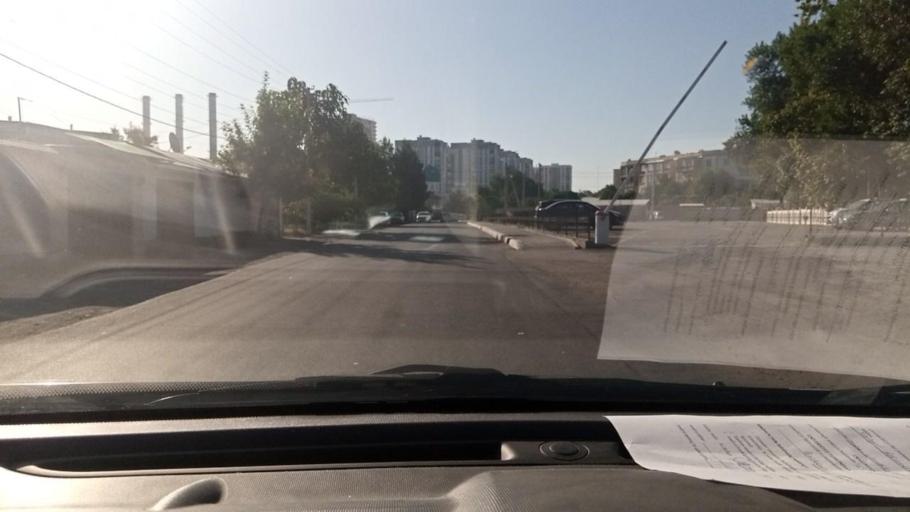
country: UZ
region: Toshkent
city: Salor
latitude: 41.3247
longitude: 69.3543
